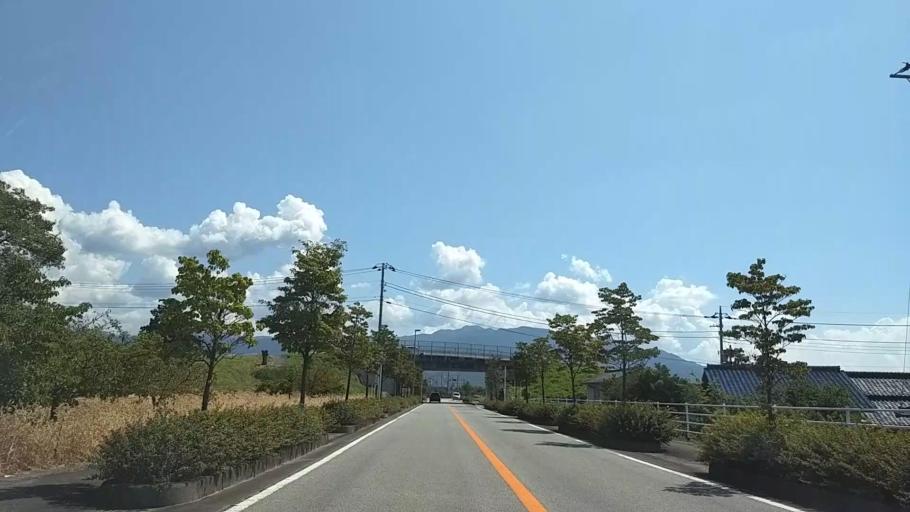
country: JP
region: Yamanashi
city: Ryuo
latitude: 35.6153
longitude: 138.5013
